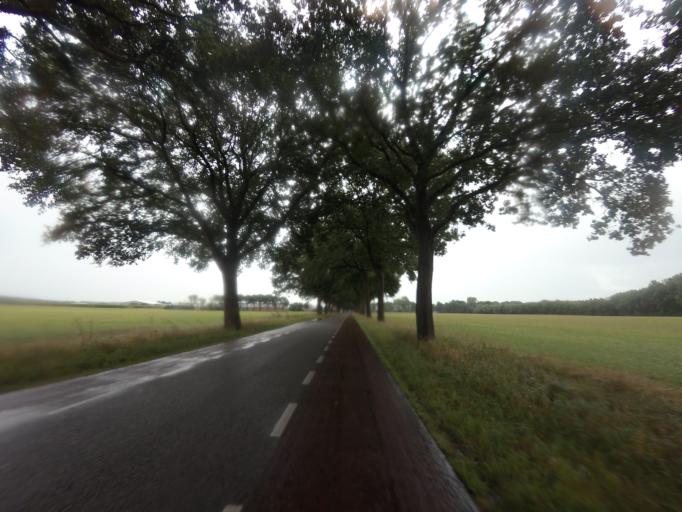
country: NL
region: Drenthe
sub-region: Gemeente Hoogeveen
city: Hoogeveen
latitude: 52.6102
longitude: 6.3955
